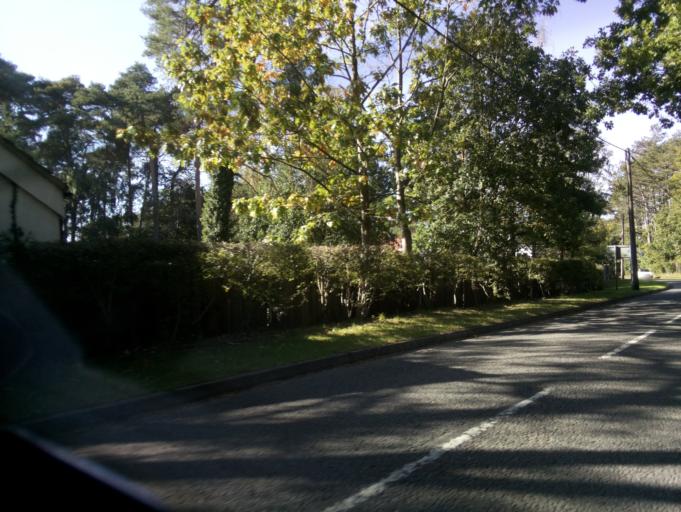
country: GB
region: England
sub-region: West Berkshire
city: Cold Ash
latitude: 51.4386
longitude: -1.2731
